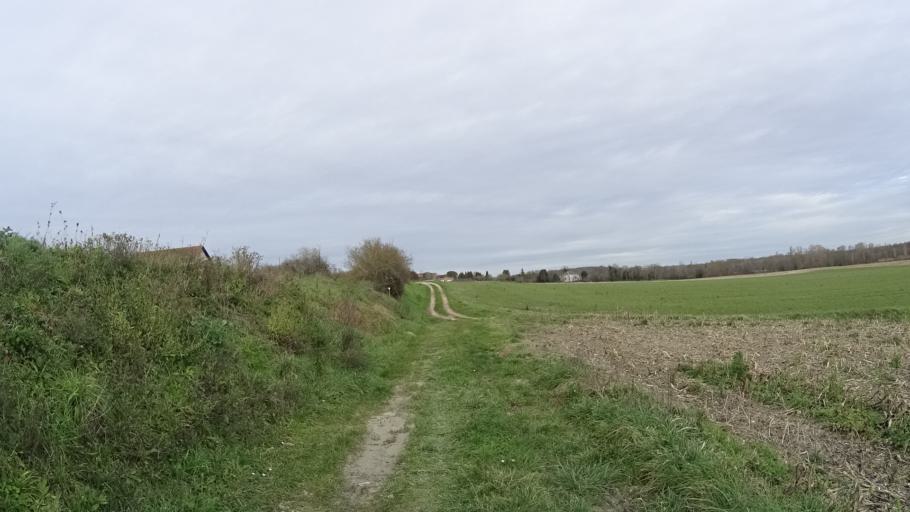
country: FR
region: Aquitaine
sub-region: Departement de la Dordogne
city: Saint-Aulaye
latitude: 45.2602
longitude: 0.1677
